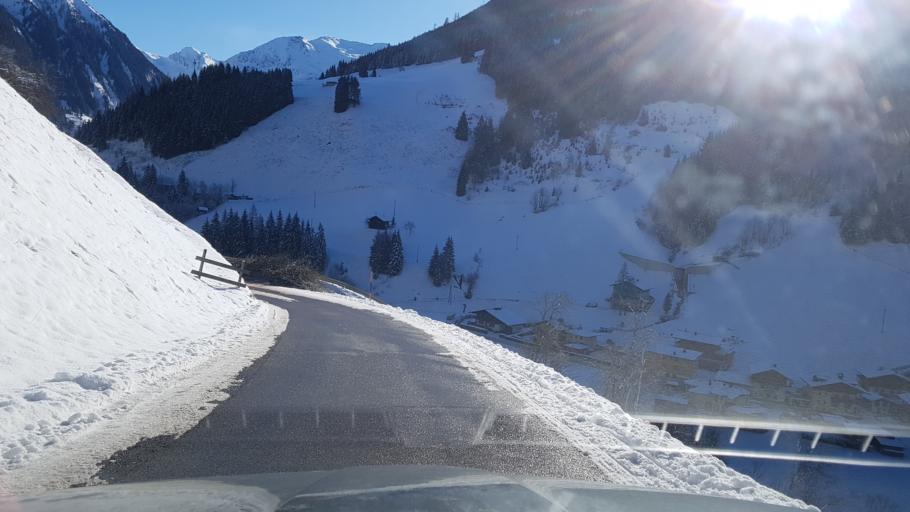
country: AT
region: Salzburg
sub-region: Politischer Bezirk Sankt Johann im Pongau
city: Huttschlag
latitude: 47.1679
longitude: 13.2663
